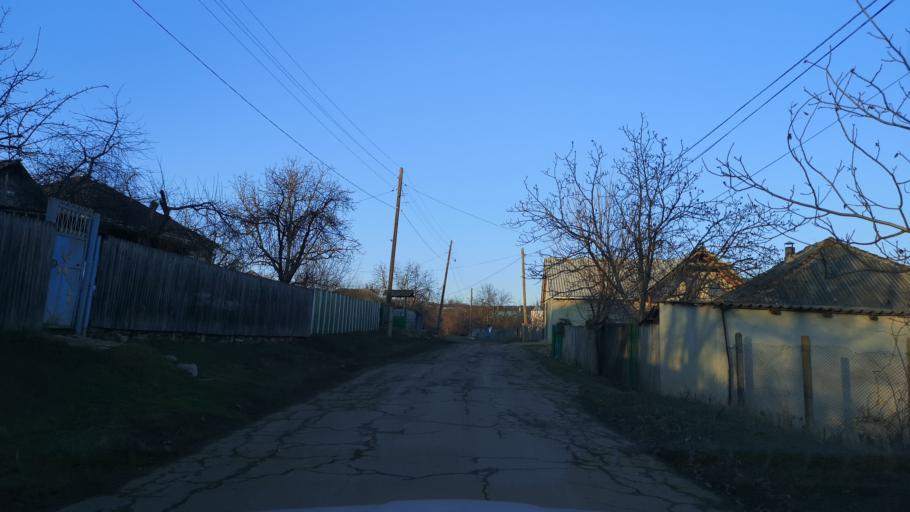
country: MD
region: Orhei
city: Orhei
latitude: 47.3649
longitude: 28.6901
